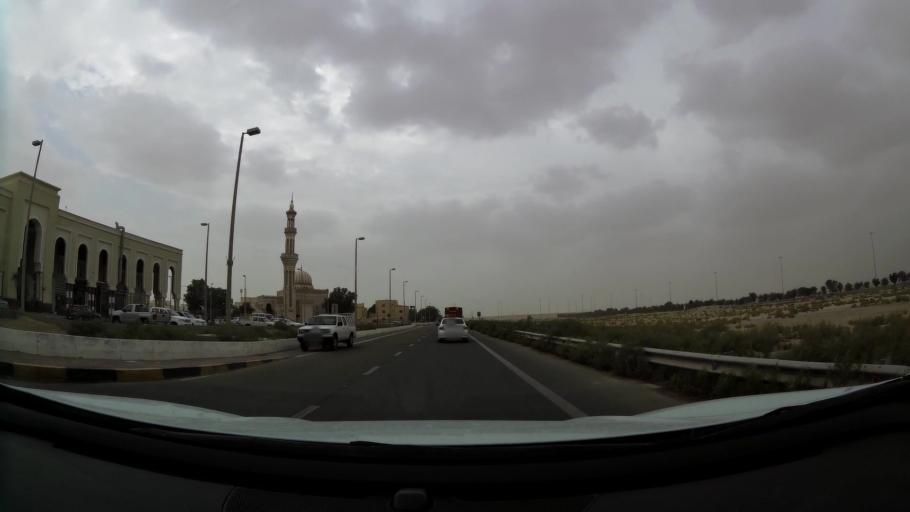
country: AE
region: Abu Dhabi
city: Abu Dhabi
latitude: 24.3754
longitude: 54.6597
